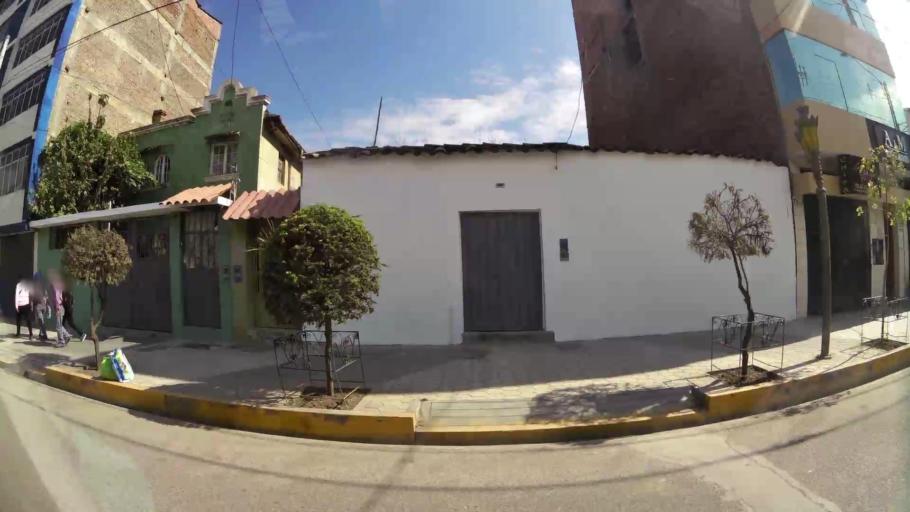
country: PE
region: Junin
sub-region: Provincia de Huancayo
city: Huancayo
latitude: -12.0643
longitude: -75.2022
